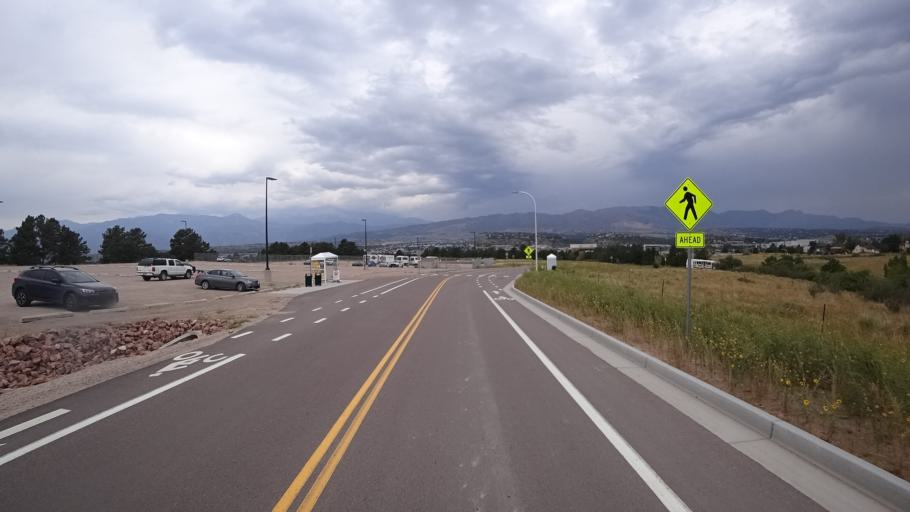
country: US
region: Colorado
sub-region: El Paso County
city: Colorado Springs
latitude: 38.9000
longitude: -104.8102
